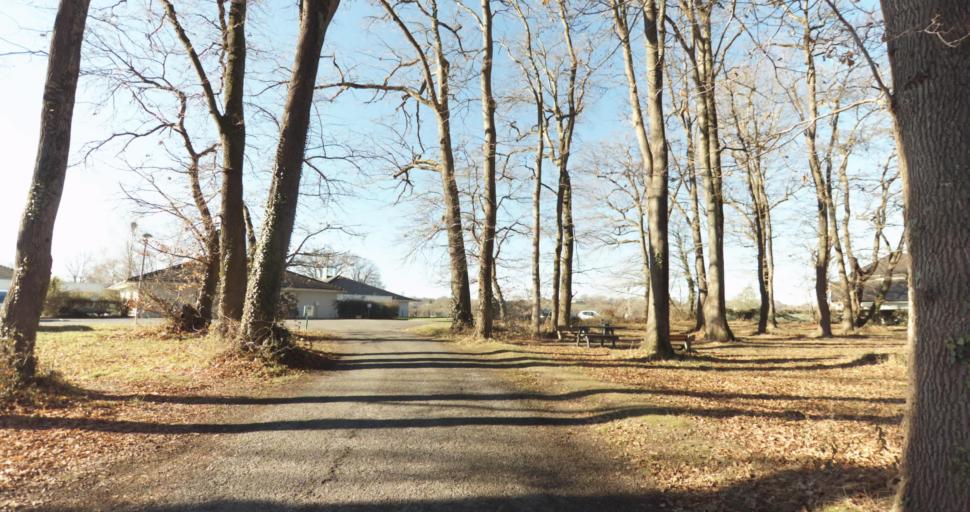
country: FR
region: Aquitaine
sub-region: Departement des Pyrenees-Atlantiques
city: Morlaas
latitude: 43.3569
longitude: -0.2664
